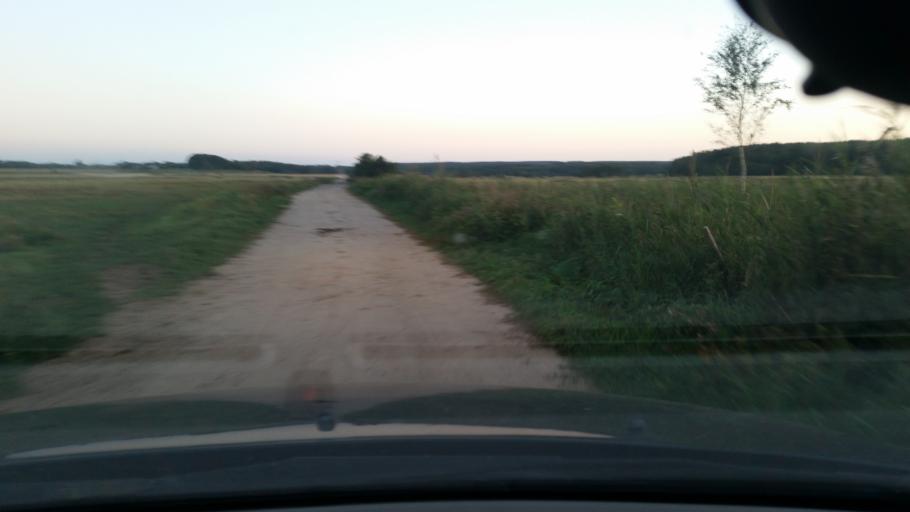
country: PL
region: Pomeranian Voivodeship
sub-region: Powiat wejherowski
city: Choczewo
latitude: 54.7844
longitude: 17.7943
